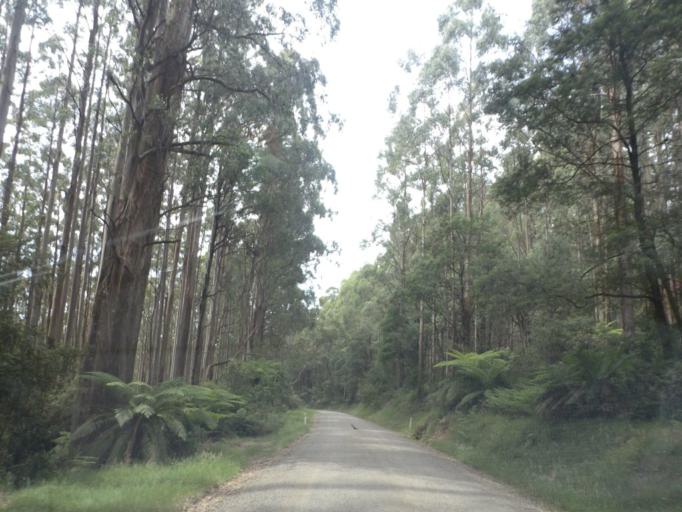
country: AU
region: Victoria
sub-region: Yarra Ranges
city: Healesville
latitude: -37.5058
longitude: 145.5309
